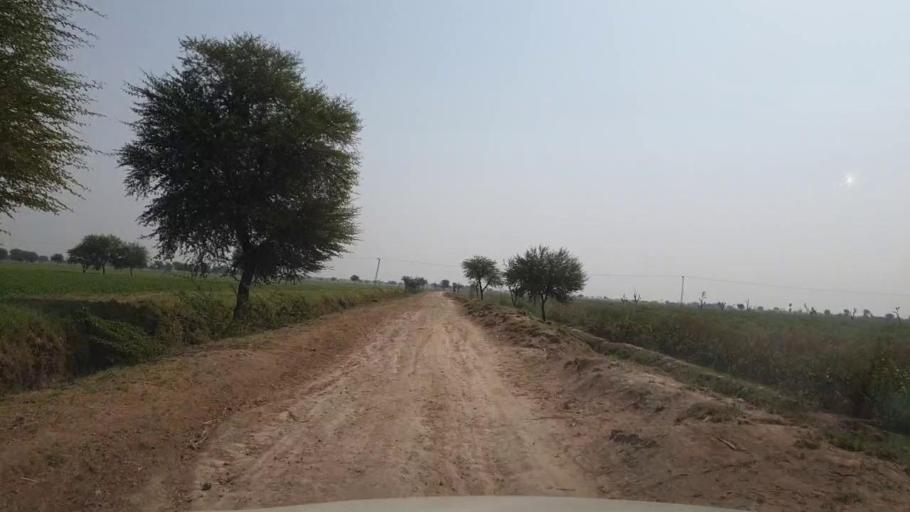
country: PK
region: Sindh
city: Chor
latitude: 25.4574
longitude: 69.6793
